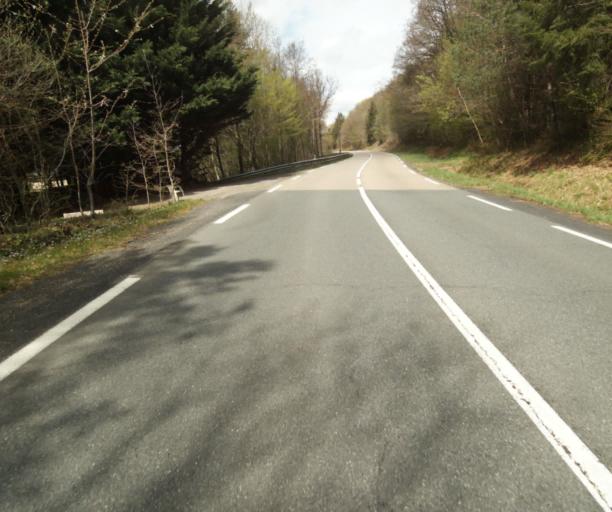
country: FR
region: Limousin
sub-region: Departement de la Correze
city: Sainte-Fortunade
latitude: 45.1951
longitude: 1.8372
